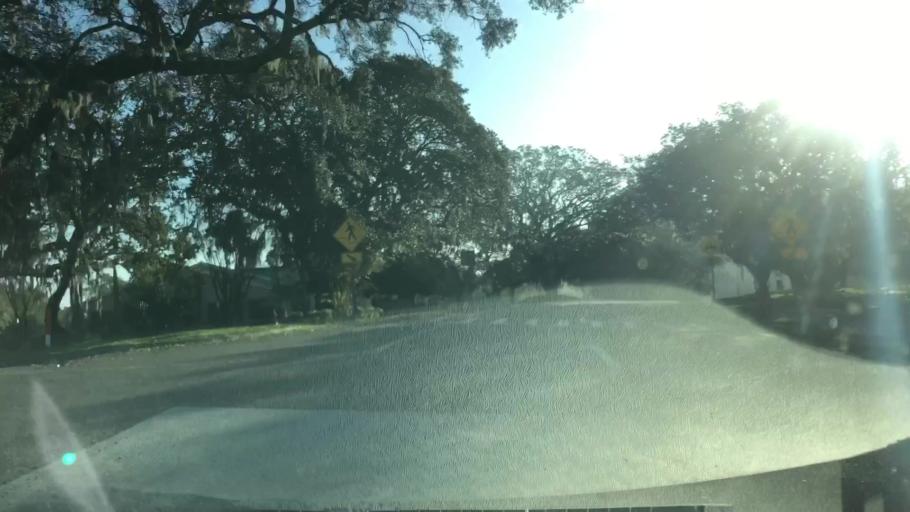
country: US
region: Florida
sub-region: Seminole County
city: Heathrow
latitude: 28.7863
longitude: -81.3457
